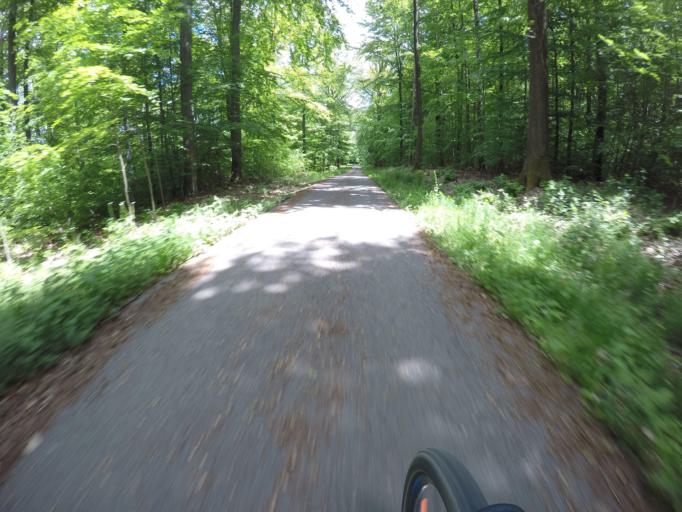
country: DE
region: Baden-Wuerttemberg
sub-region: Regierungsbezirk Stuttgart
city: Sindelfingen
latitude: 48.7388
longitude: 9.0410
